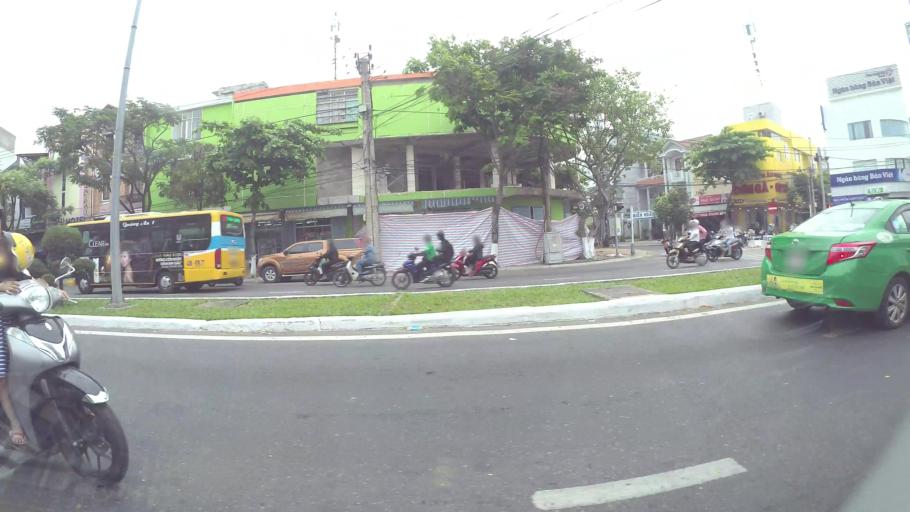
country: VN
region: Da Nang
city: Da Nang
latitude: 16.0459
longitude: 108.2097
